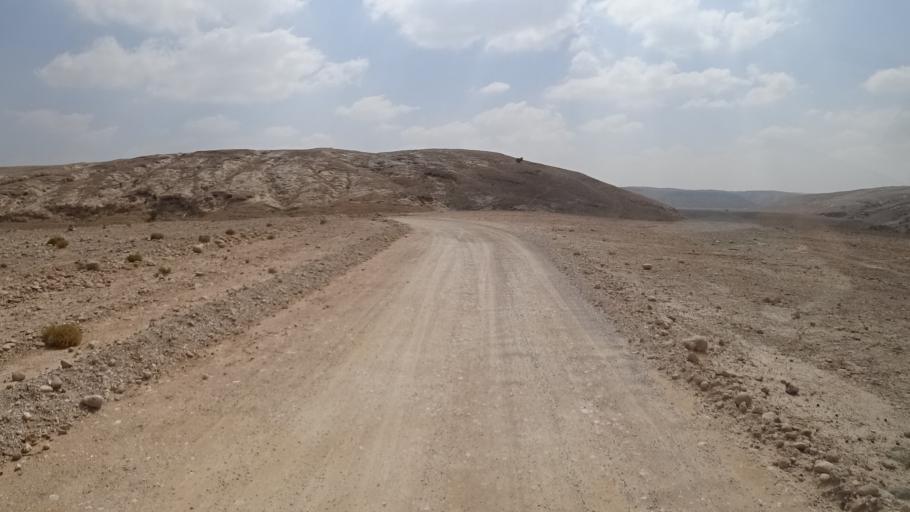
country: OM
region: Zufar
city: Salalah
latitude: 17.2366
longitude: 53.8968
